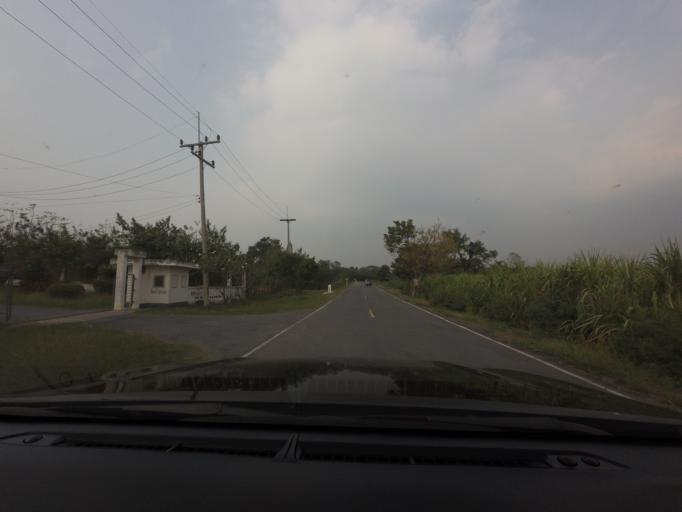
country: TH
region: Sara Buri
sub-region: Amphoe Wang Muang
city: Wang Muang
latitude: 14.8468
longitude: 101.1016
